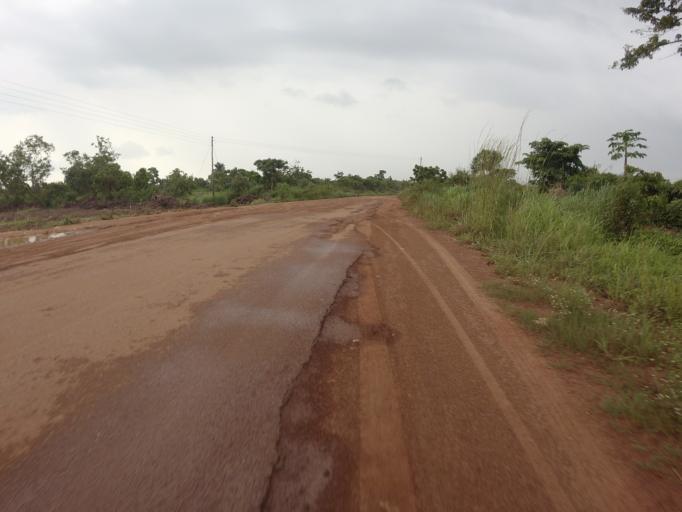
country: GH
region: Volta
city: Kpandu
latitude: 7.0102
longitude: 0.4288
